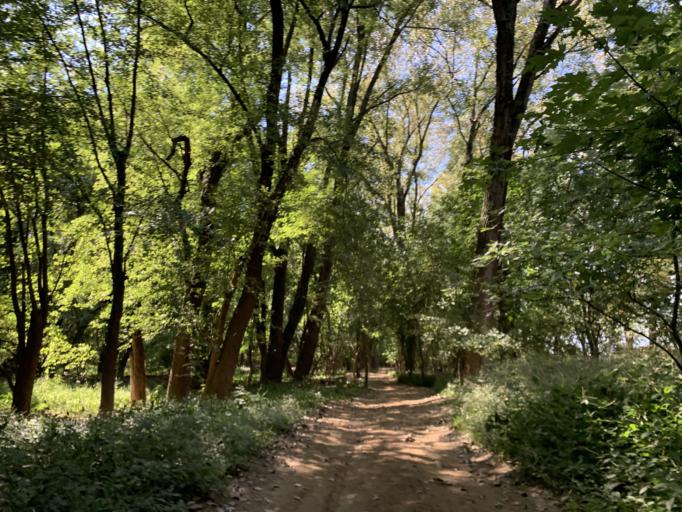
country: US
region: Indiana
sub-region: Floyd County
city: New Albany
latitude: 38.2797
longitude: -85.8067
